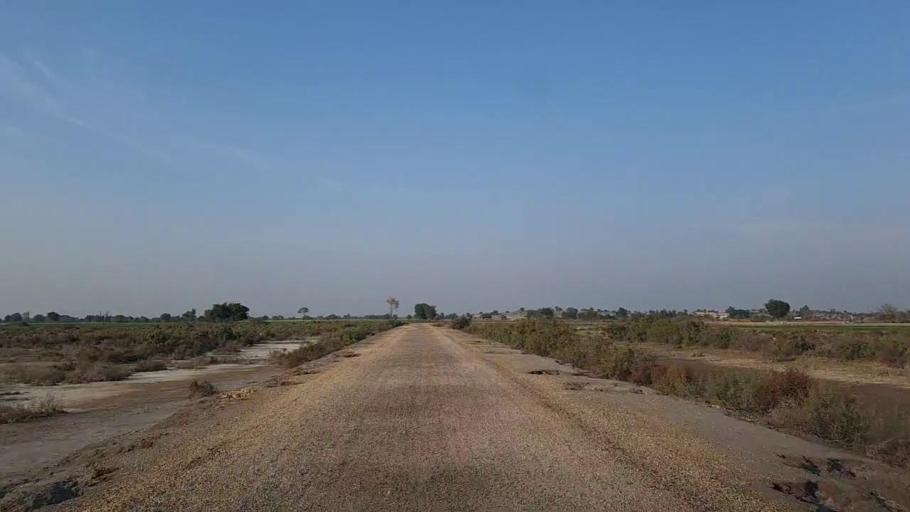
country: PK
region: Sindh
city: Jam Sahib
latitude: 26.3743
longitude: 68.5273
